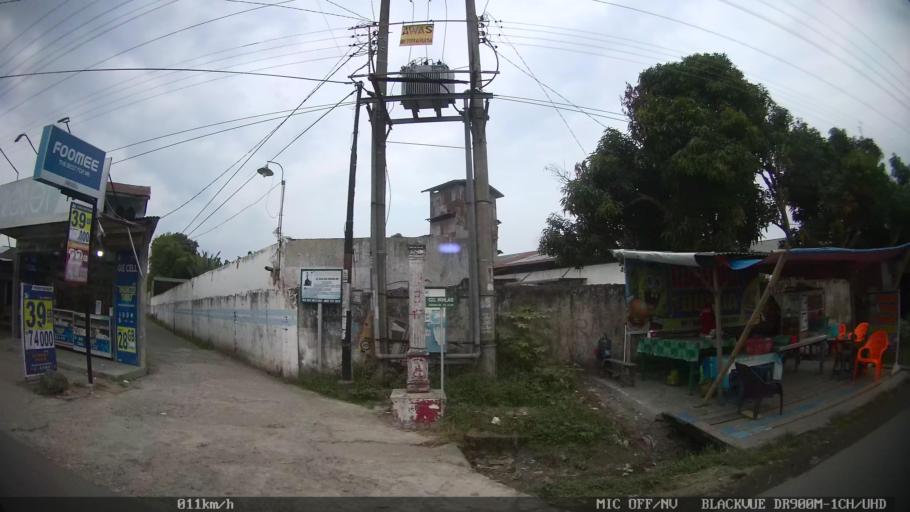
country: ID
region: North Sumatra
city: Sunggal
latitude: 3.5677
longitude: 98.5803
